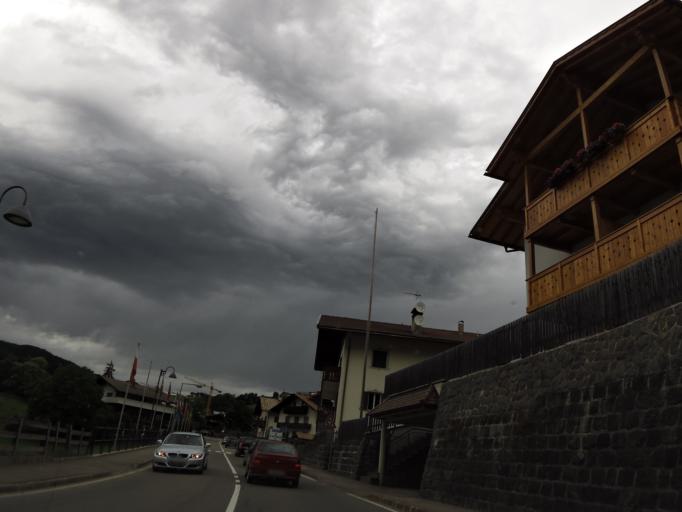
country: IT
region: Trentino-Alto Adige
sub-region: Bolzano
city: Siusi
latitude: 46.5426
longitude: 11.5624
